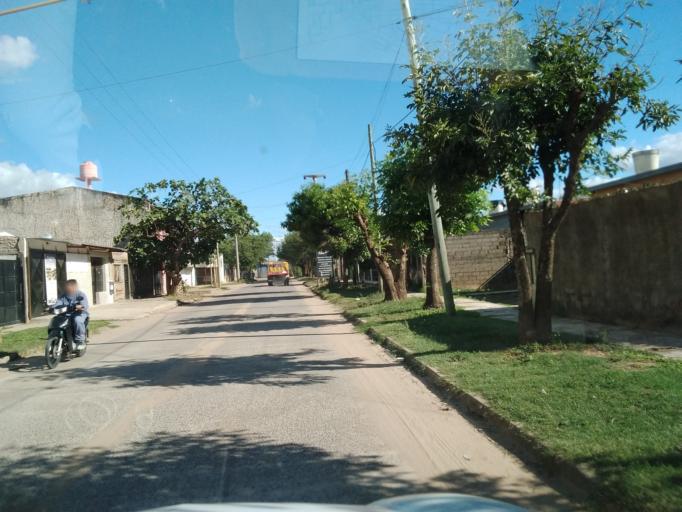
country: AR
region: Corrientes
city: Corrientes
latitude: -27.5049
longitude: -58.8048
